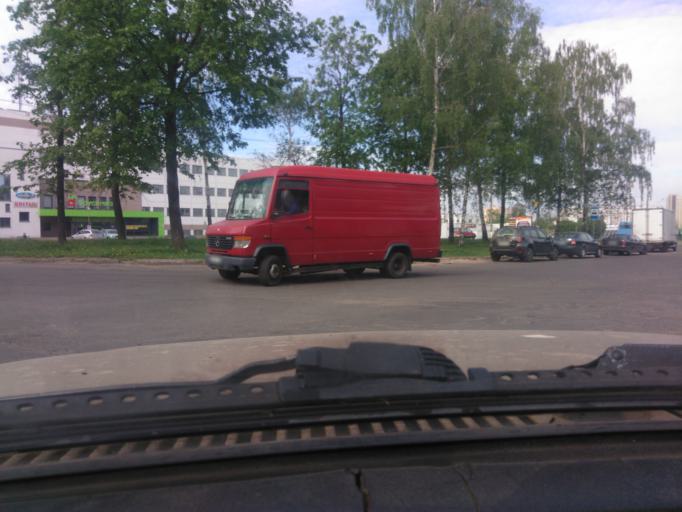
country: BY
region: Mogilev
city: Mahilyow
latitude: 53.9186
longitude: 30.3073
